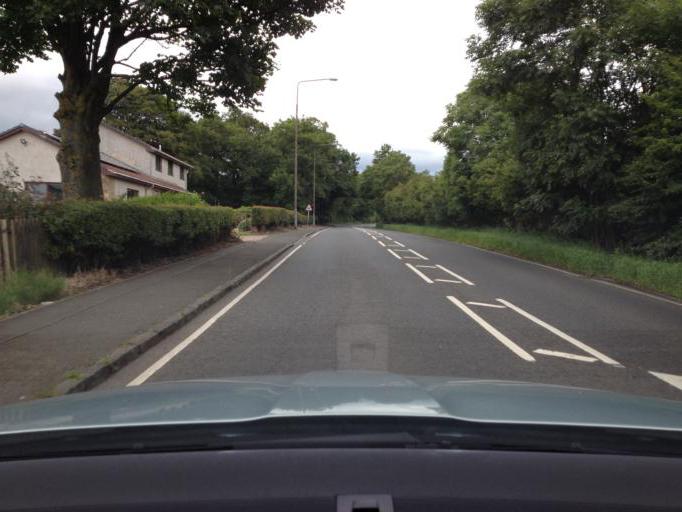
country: GB
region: Scotland
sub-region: West Lothian
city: Blackburn
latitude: 55.8735
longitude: -3.6030
